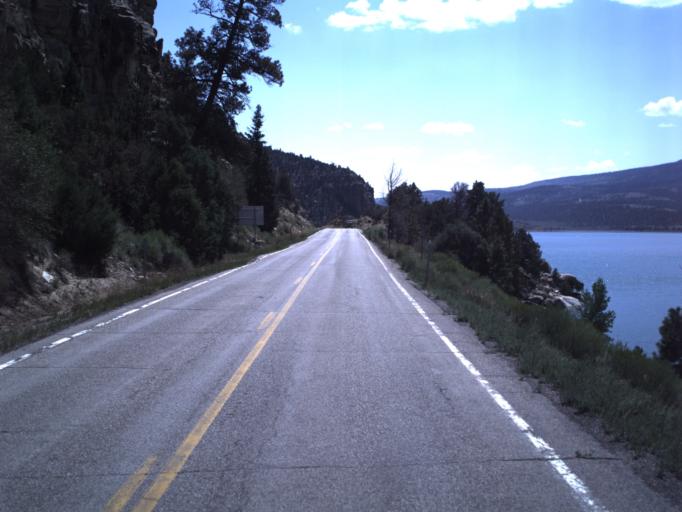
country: US
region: Utah
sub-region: Emery County
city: Orangeville
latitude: 39.2988
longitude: -111.2718
